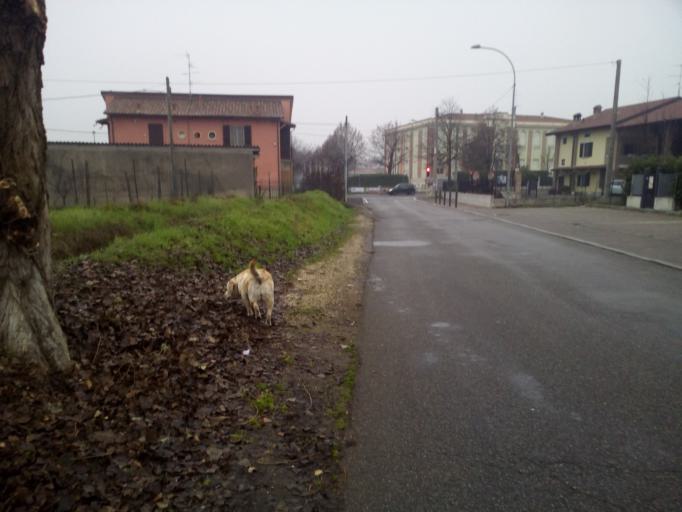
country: IT
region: Lombardy
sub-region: Provincia di Brescia
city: Castel Mella
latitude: 45.5112
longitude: 10.1465
